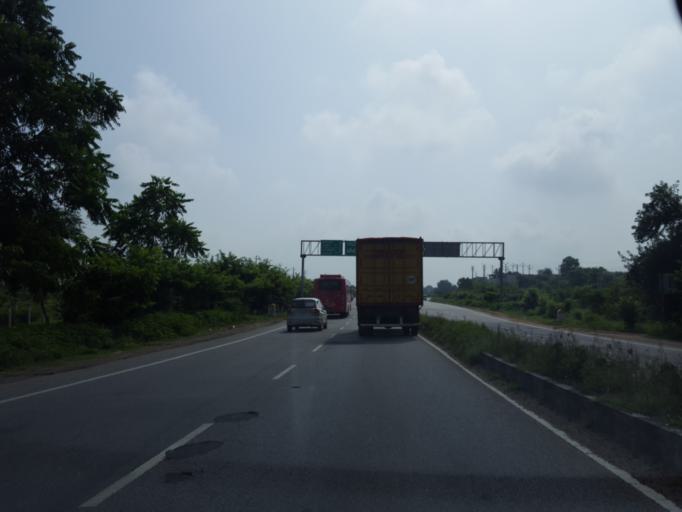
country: IN
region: Telangana
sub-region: Rangareddi
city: Ghatkesar
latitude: 17.2846
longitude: 78.7776
